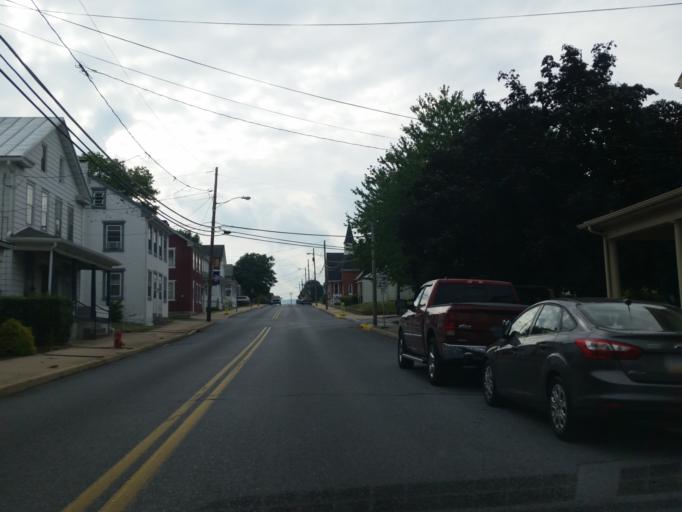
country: US
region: Pennsylvania
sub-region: Lebanon County
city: Richland
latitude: 40.3568
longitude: -76.2552
